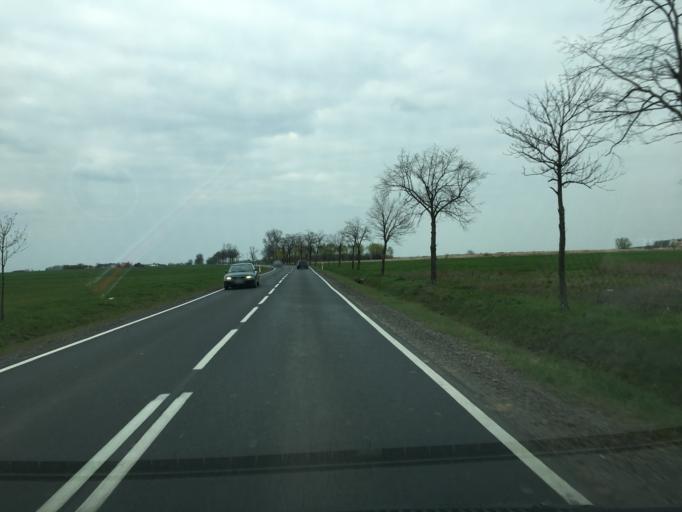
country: PL
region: Lower Silesian Voivodeship
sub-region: Powiat legnicki
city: Prochowice
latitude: 51.2600
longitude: 16.3324
